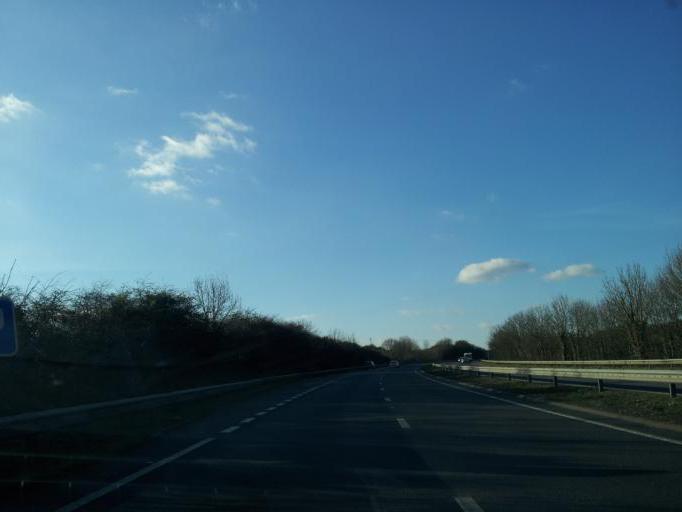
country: GB
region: England
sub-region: Devon
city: Exeter
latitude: 50.7079
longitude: -3.5648
